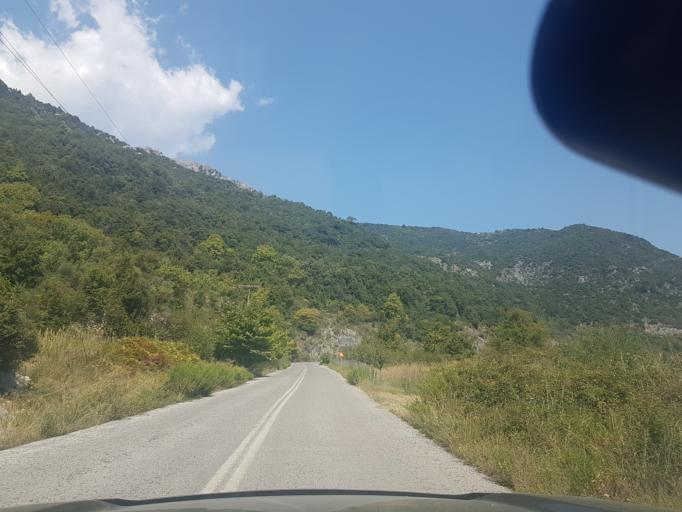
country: GR
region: Central Greece
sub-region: Nomos Evvoias
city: Yimnon
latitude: 38.6334
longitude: 23.8908
